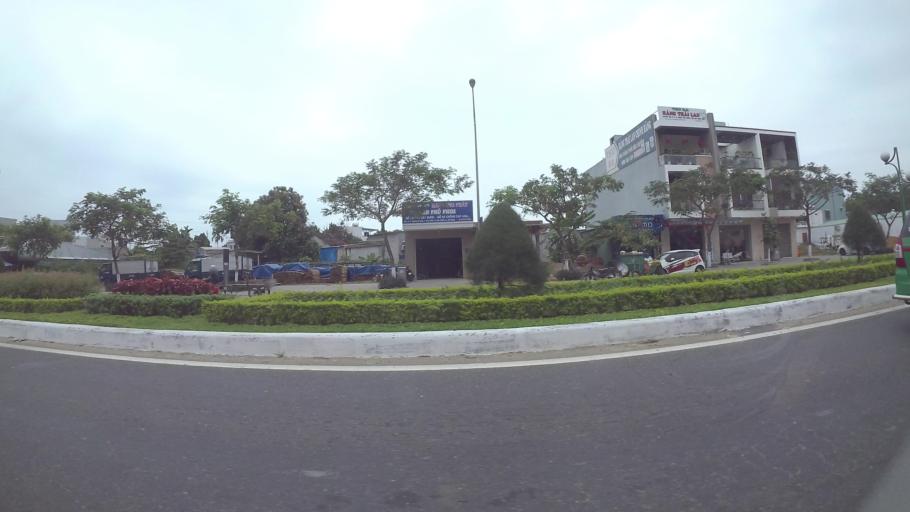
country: VN
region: Da Nang
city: Lien Chieu
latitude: 16.0652
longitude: 108.1735
